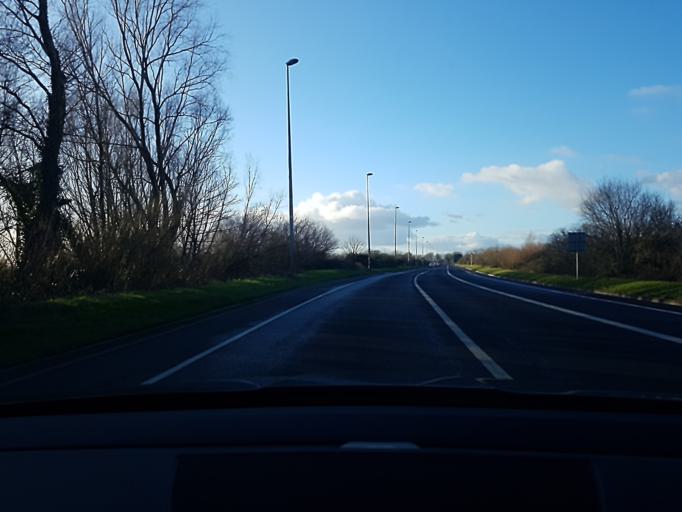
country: IE
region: Munster
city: Moyross
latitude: 52.6595
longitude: -8.6584
